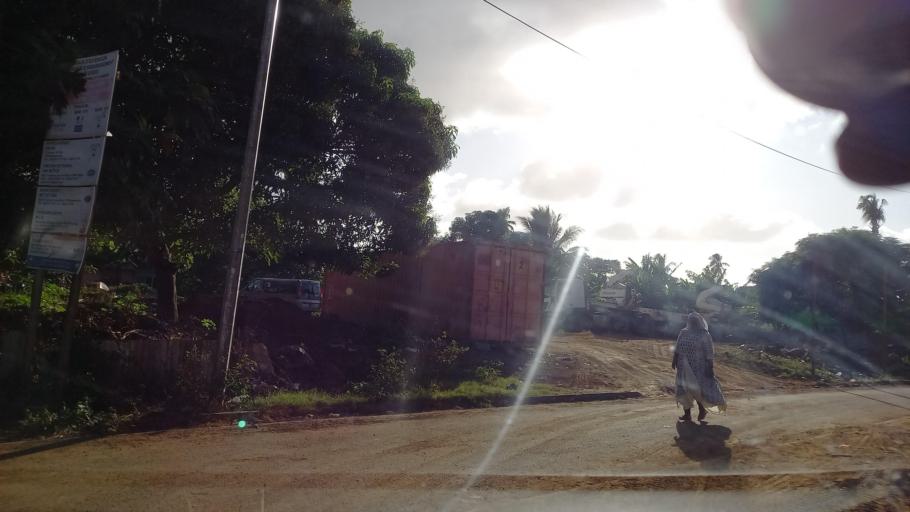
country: YT
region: Bandrele
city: Bandrele
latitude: -12.9135
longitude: 45.1937
